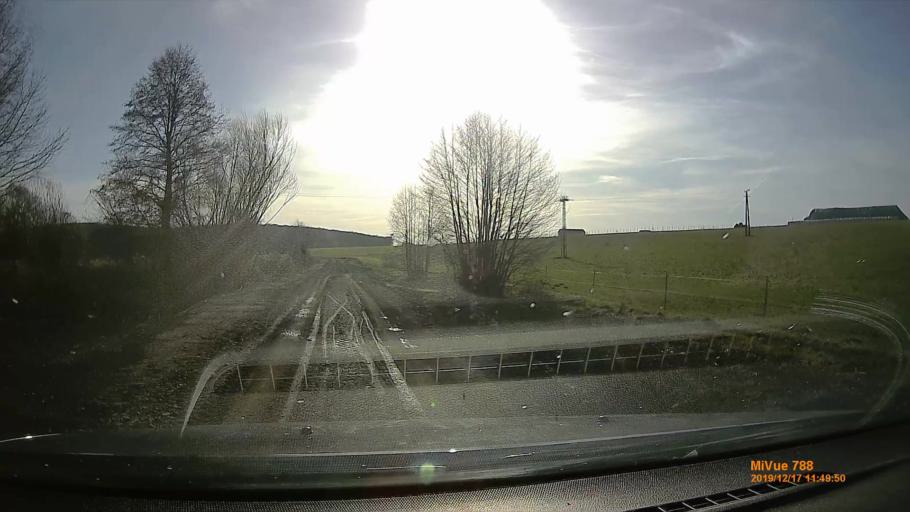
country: HU
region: Somogy
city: Kaposvar
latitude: 46.4545
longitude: 17.7685
